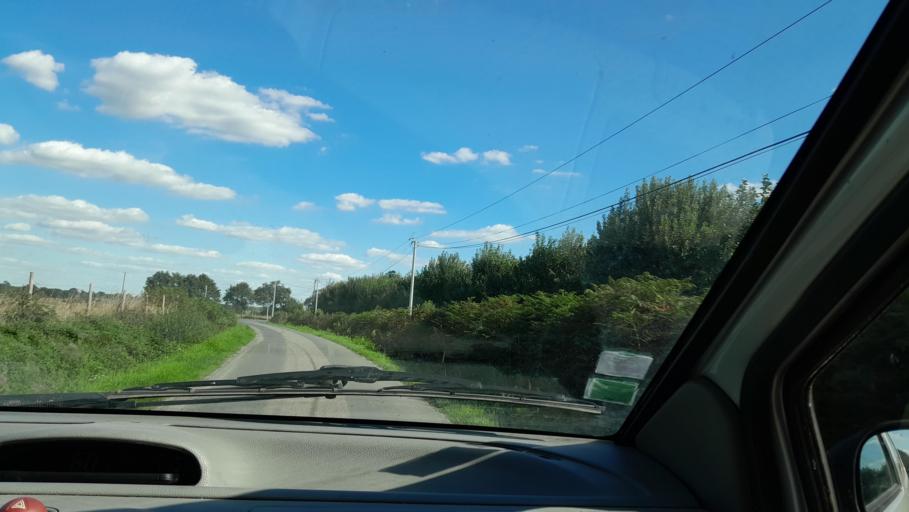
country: FR
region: Pays de la Loire
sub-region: Departement de la Mayenne
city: Ballots
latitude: 47.9534
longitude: -1.0666
